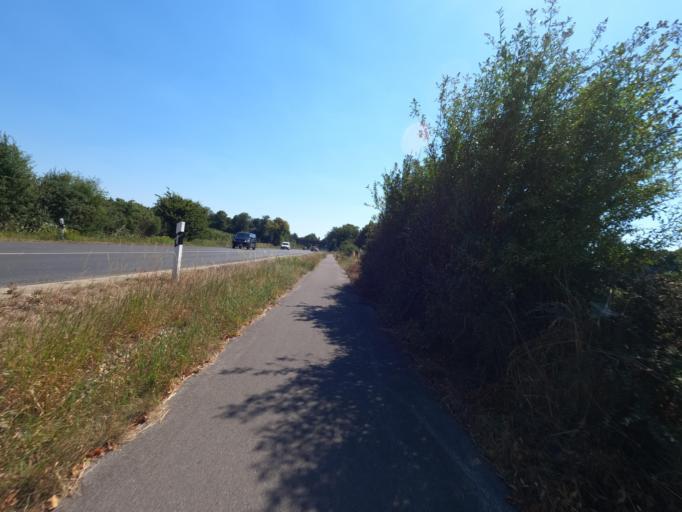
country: DE
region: North Rhine-Westphalia
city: Erkelenz
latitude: 51.0905
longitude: 6.3057
